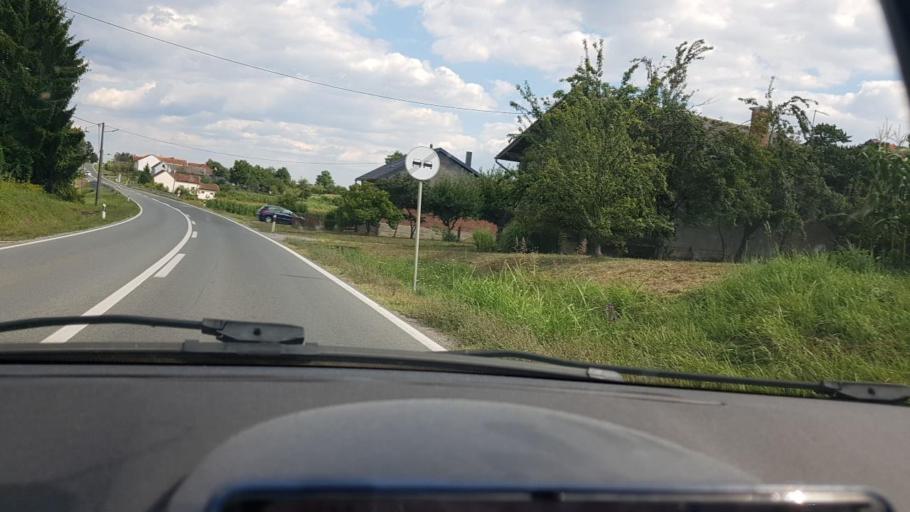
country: HR
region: Bjelovarsko-Bilogorska
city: Zdralovi
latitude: 45.8686
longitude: 16.9050
